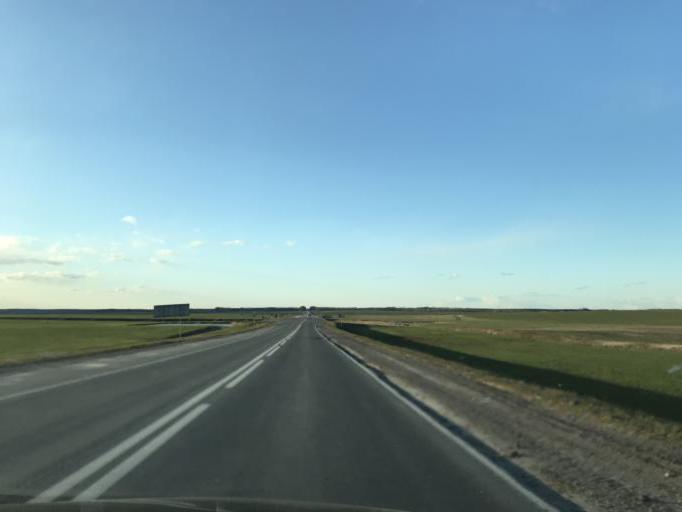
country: BY
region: Gomel
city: Kastsyukowka
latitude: 52.6878
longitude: 30.8108
